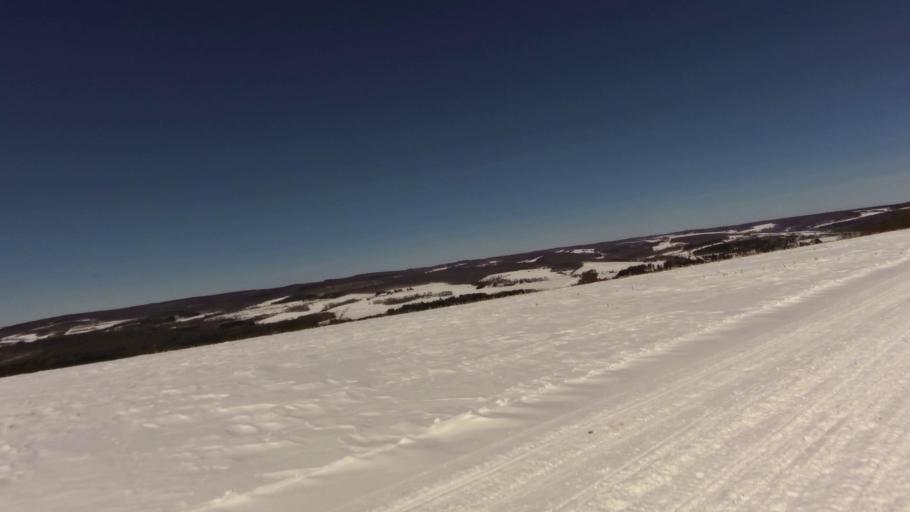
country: US
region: New York
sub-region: Allegany County
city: Houghton
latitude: 42.3656
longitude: -78.2562
